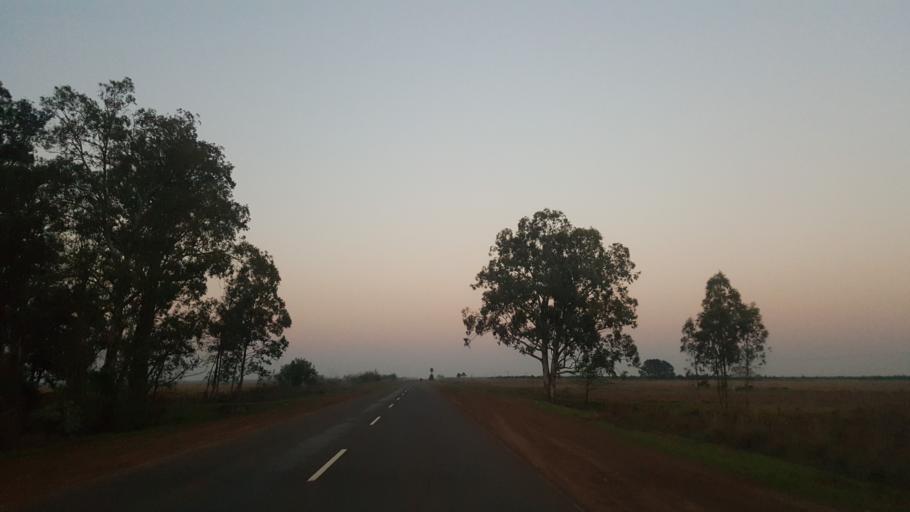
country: PY
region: Itapua
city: San Cosme y Damian
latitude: -27.5408
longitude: -56.2035
